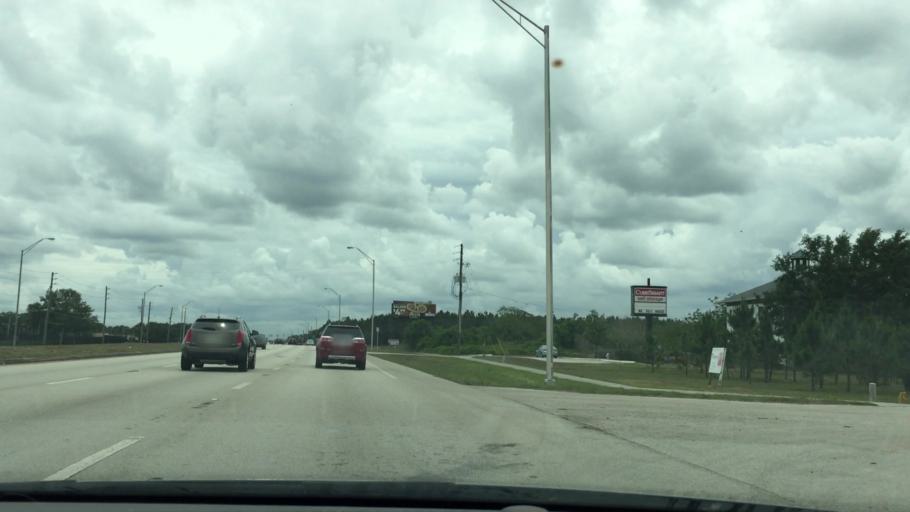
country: US
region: Florida
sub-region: Osceola County
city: Buenaventura Lakes
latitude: 28.2964
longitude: -81.3699
